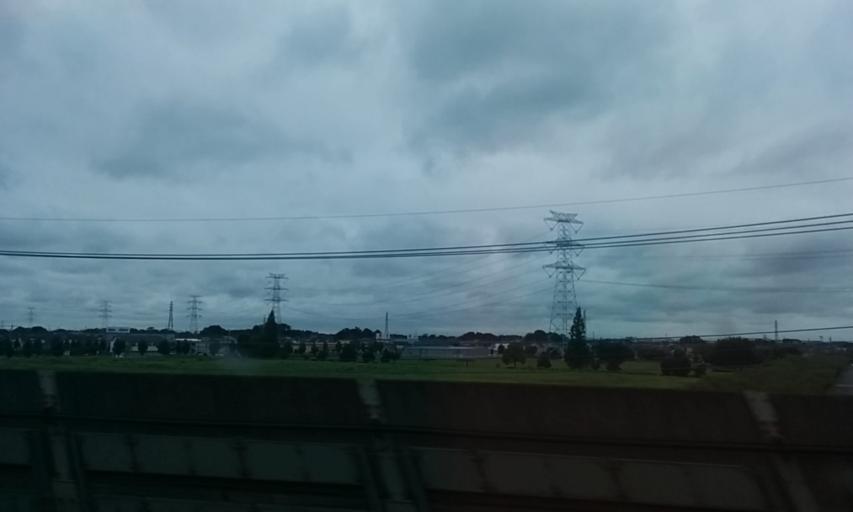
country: JP
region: Saitama
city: Kurihashi
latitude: 36.1109
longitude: 139.7061
